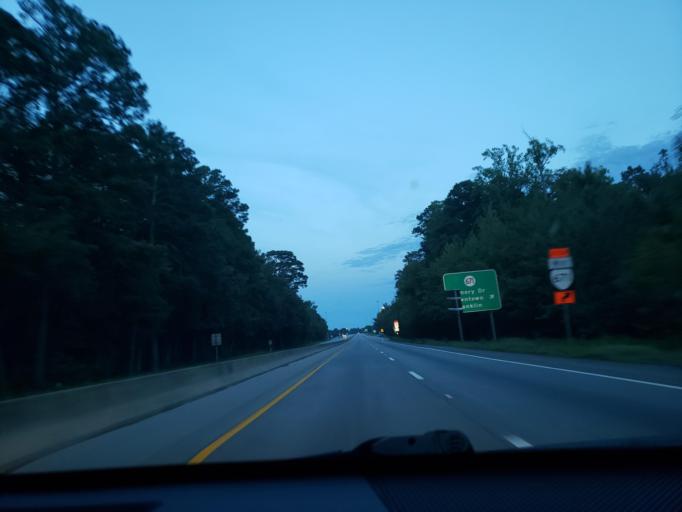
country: US
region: Virginia
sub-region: City of Franklin
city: Franklin
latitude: 36.6690
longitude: -76.9661
